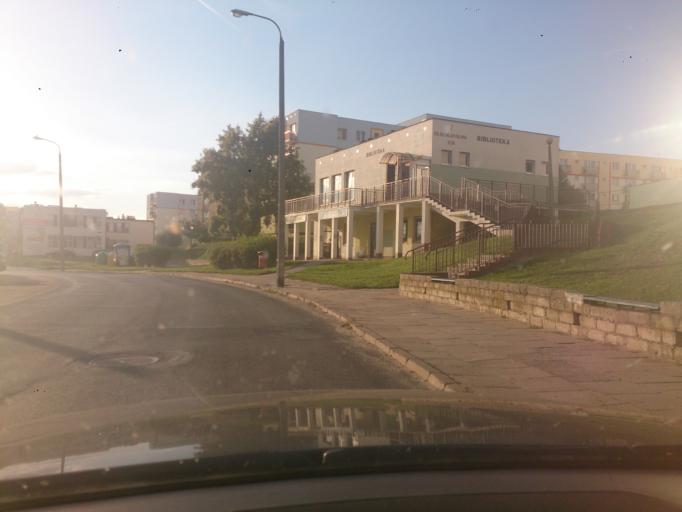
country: PL
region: Kujawsko-Pomorskie
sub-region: Grudziadz
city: Grudziadz
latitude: 53.4554
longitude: 18.7185
